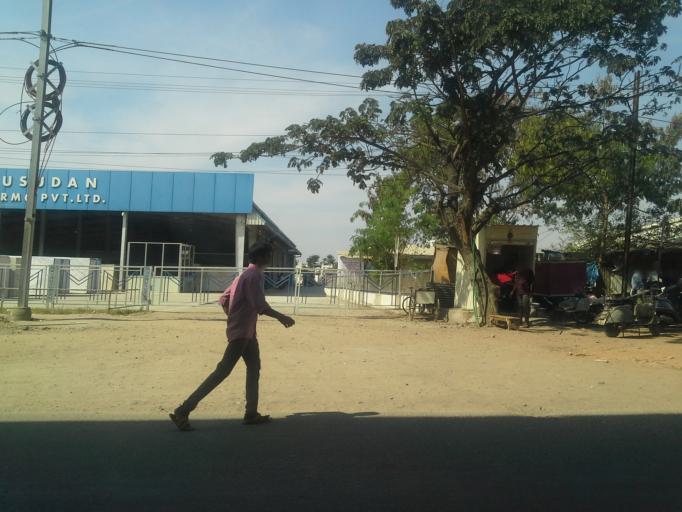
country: IN
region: Telangana
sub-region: Hyderabad
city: Hyderabad
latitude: 17.3703
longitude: 78.4292
